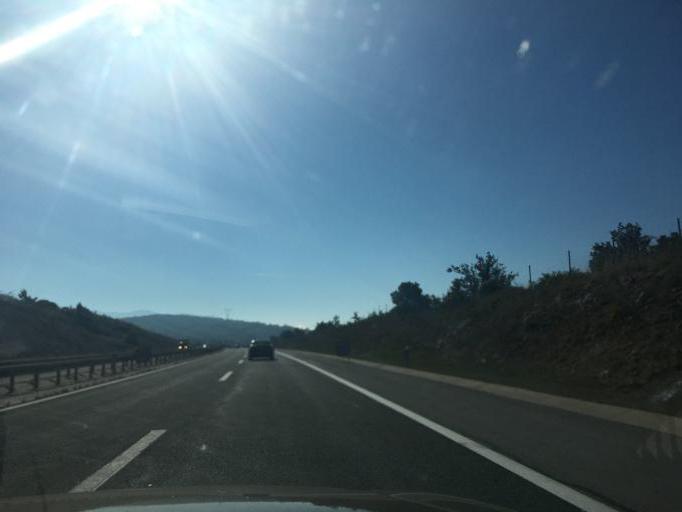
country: HR
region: Licko-Senjska
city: Gospic
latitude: 44.6562
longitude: 15.4284
